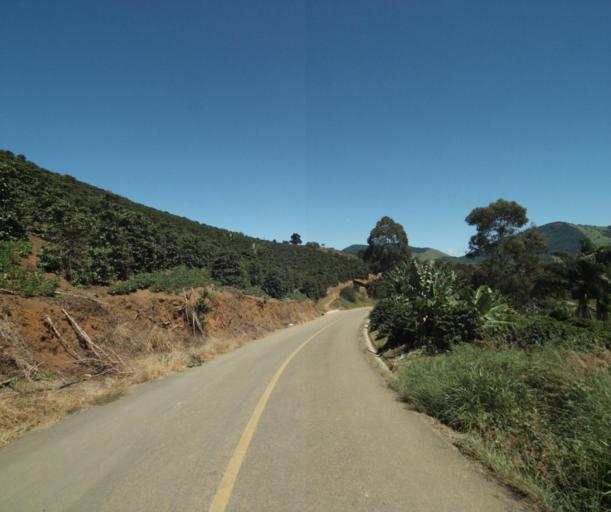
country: BR
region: Minas Gerais
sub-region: Espera Feliz
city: Espera Feliz
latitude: -20.6091
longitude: -41.8337
